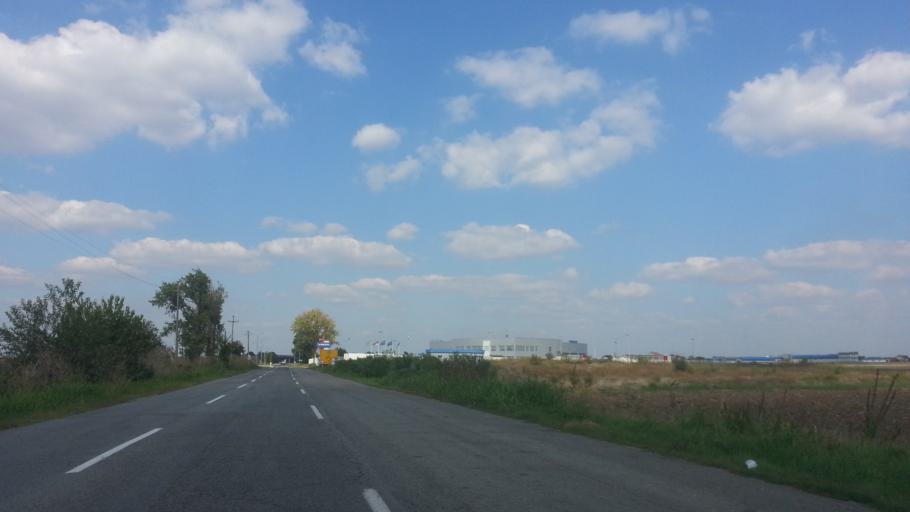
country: RS
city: Novi Banovci
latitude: 44.9385
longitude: 20.2810
